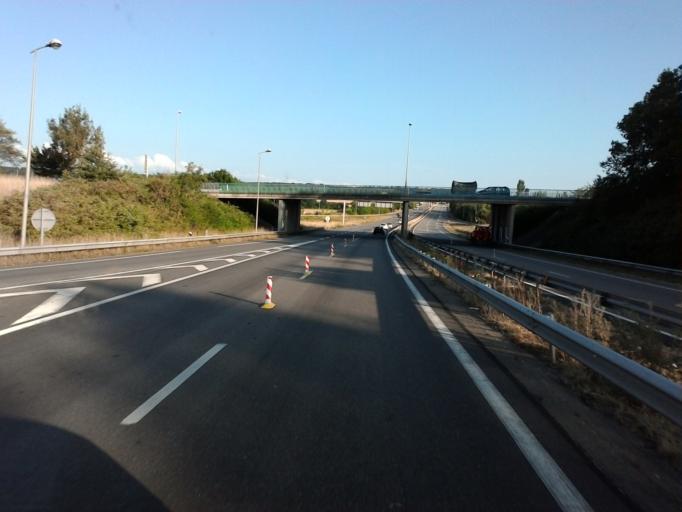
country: FR
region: Lorraine
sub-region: Departement des Vosges
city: Epinal
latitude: 48.1981
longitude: 6.4726
